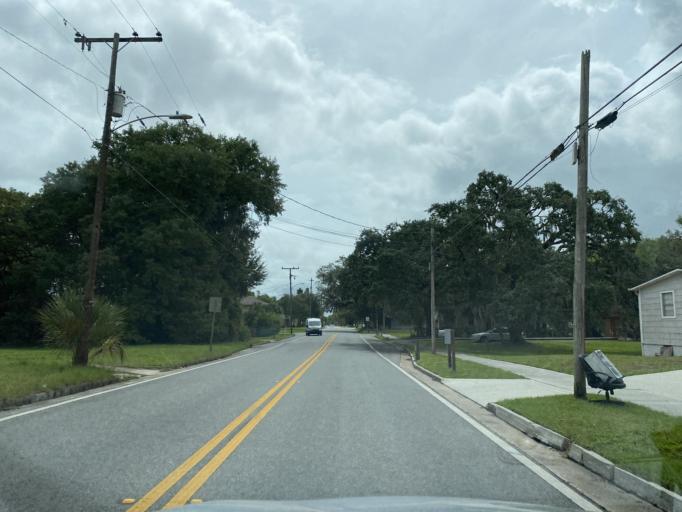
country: US
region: Florida
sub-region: Seminole County
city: Sanford
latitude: 28.8104
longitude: -81.2624
